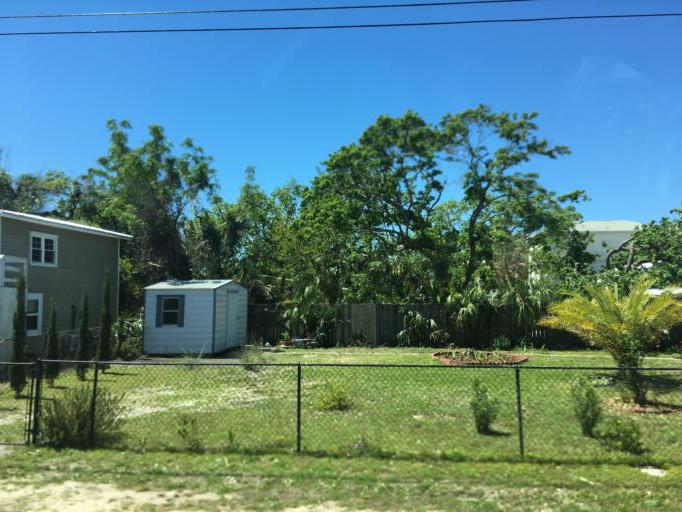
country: US
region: Florida
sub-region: Bay County
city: Laguna Beach
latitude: 30.2397
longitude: -85.9202
